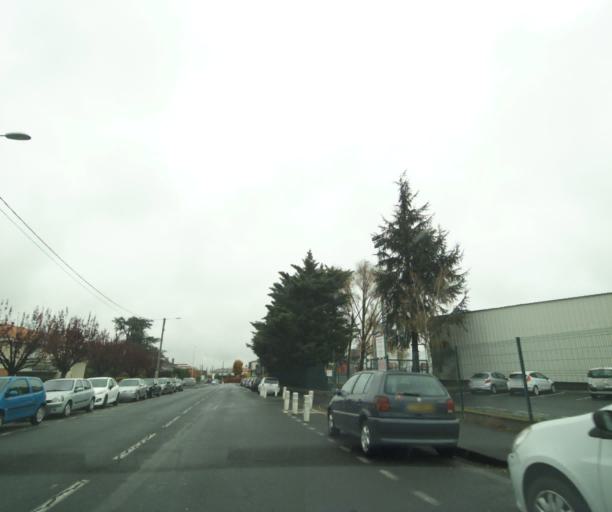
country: FR
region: Auvergne
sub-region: Departement du Puy-de-Dome
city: Aubiere
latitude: 45.7594
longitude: 3.1053
